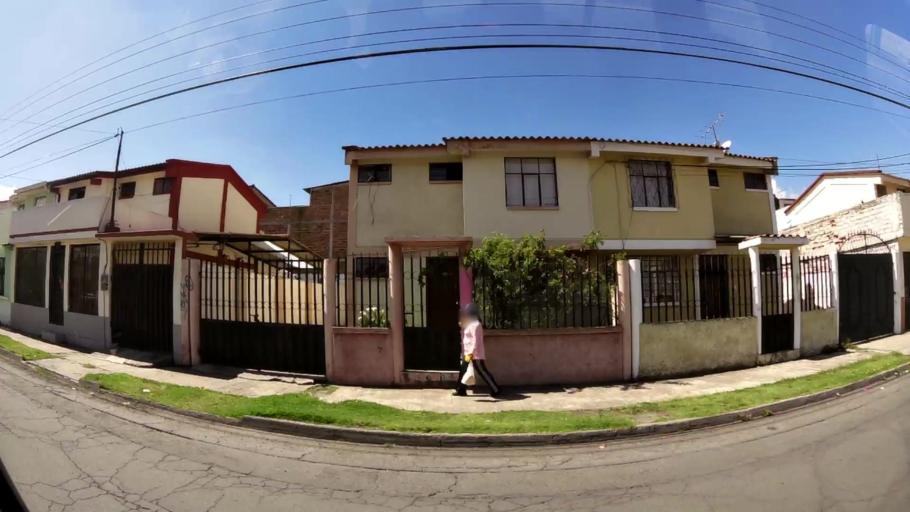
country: EC
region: Chimborazo
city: Riobamba
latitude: -1.6791
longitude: -78.6371
